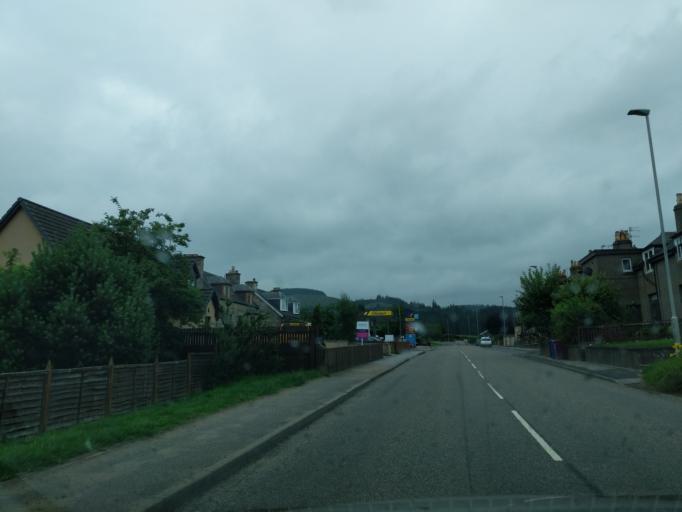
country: GB
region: Scotland
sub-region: Moray
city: Rothes
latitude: 57.4870
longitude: -3.1845
